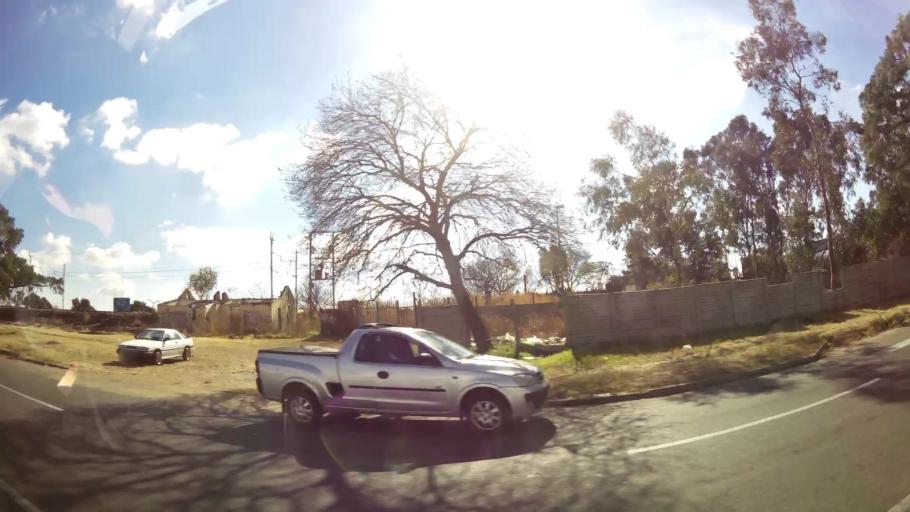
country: ZA
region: Gauteng
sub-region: City of Johannesburg Metropolitan Municipality
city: Roodepoort
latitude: -26.1273
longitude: 27.8295
